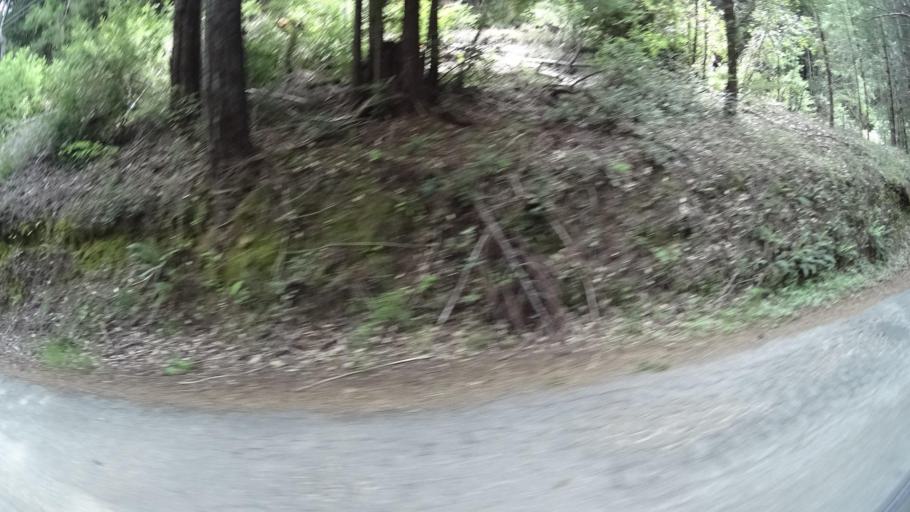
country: US
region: California
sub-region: Humboldt County
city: Redway
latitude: 40.0281
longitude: -123.9479
